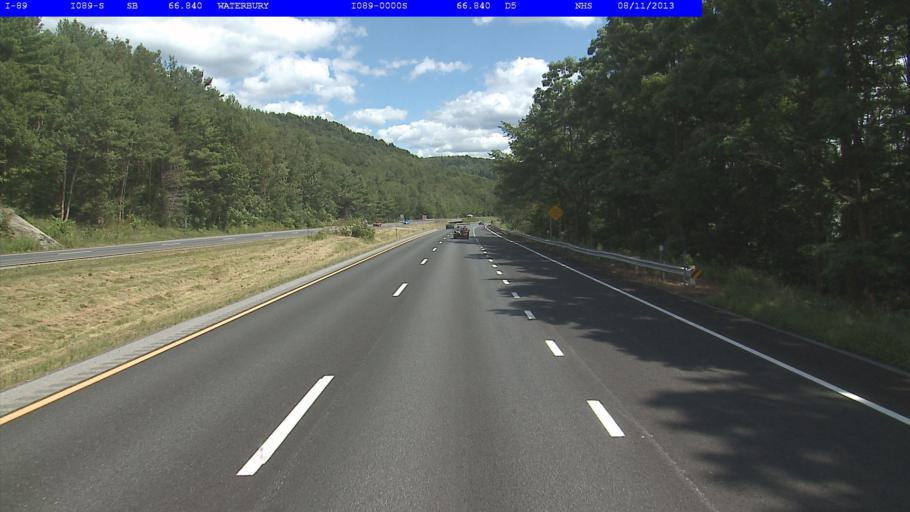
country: US
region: Vermont
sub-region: Washington County
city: Waterbury
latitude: 44.3613
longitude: -72.8071
